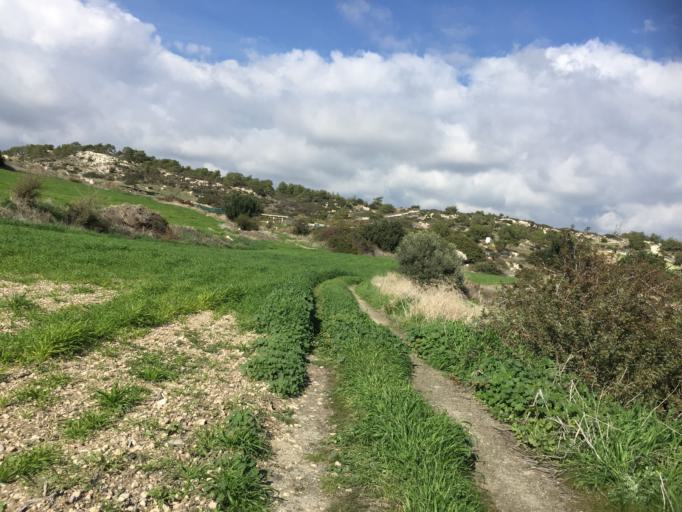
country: CY
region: Larnaka
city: Agios Tychon
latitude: 34.7410
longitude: 33.1410
